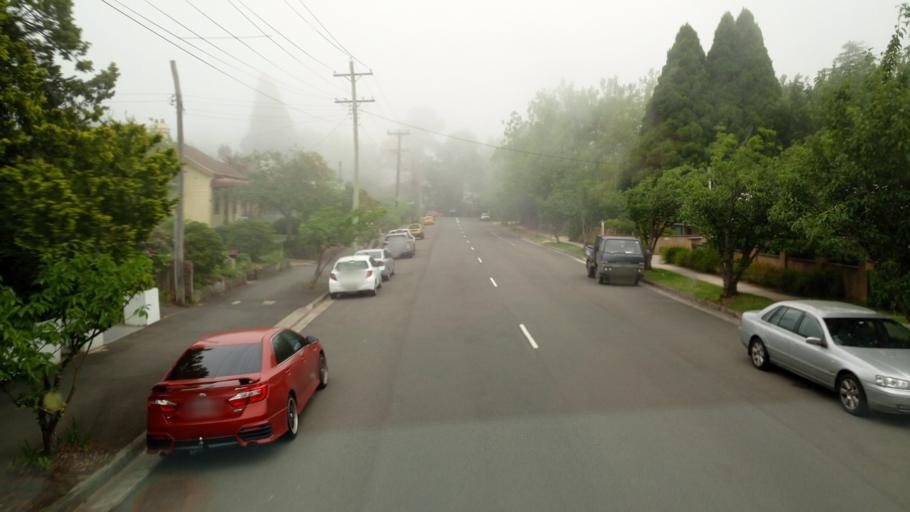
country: AU
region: New South Wales
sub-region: Blue Mountains Municipality
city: Leura
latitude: -33.7136
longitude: 150.3330
